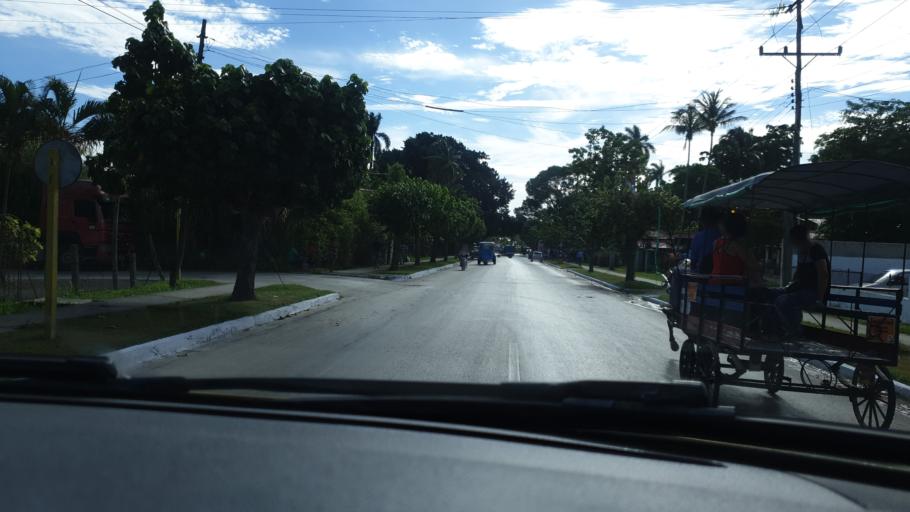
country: CU
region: Villa Clara
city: Santa Clara
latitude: 22.4148
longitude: -79.9484
